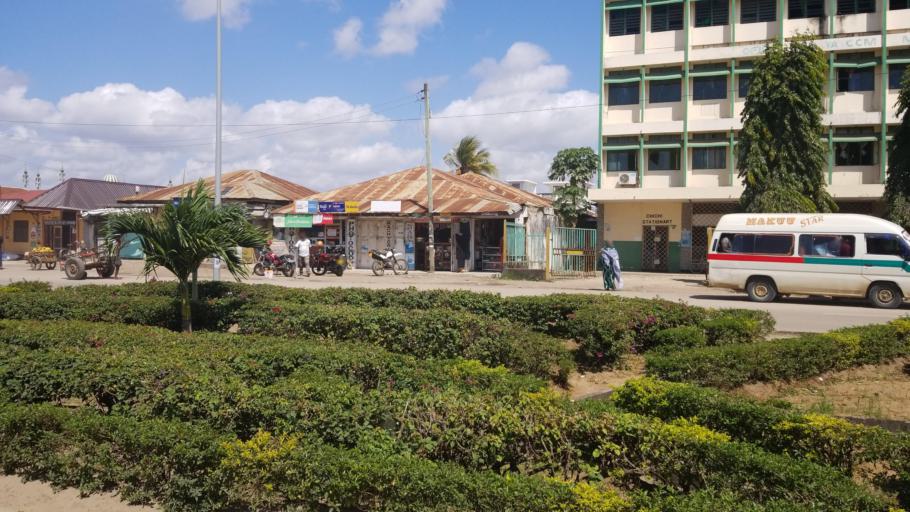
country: TZ
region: Tanga
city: Tanga
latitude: -5.0845
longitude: 39.0975
